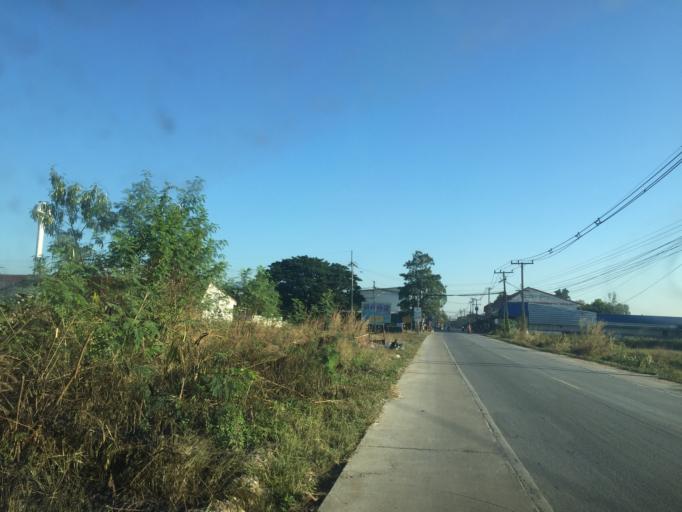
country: TH
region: Lamphun
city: Lamphun
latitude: 18.6032
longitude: 99.0530
